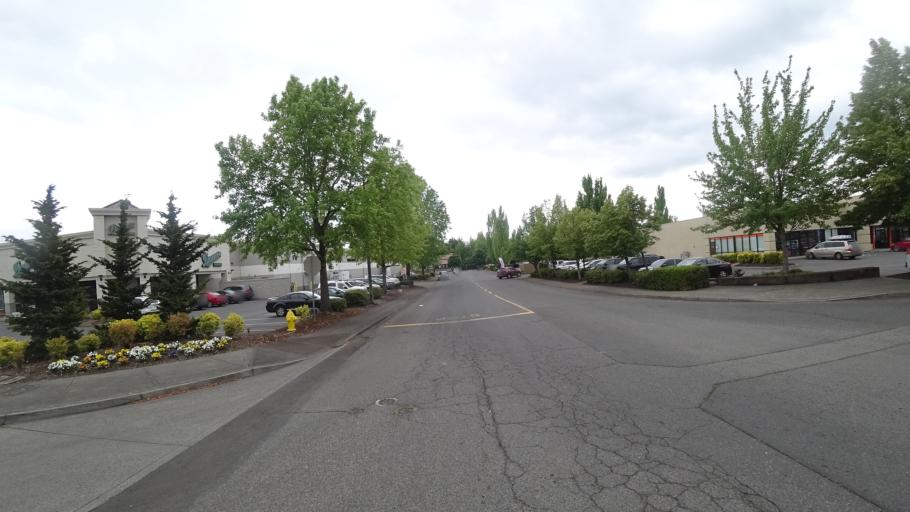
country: US
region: Oregon
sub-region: Washington County
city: Rockcreek
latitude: 45.5362
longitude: -122.8664
